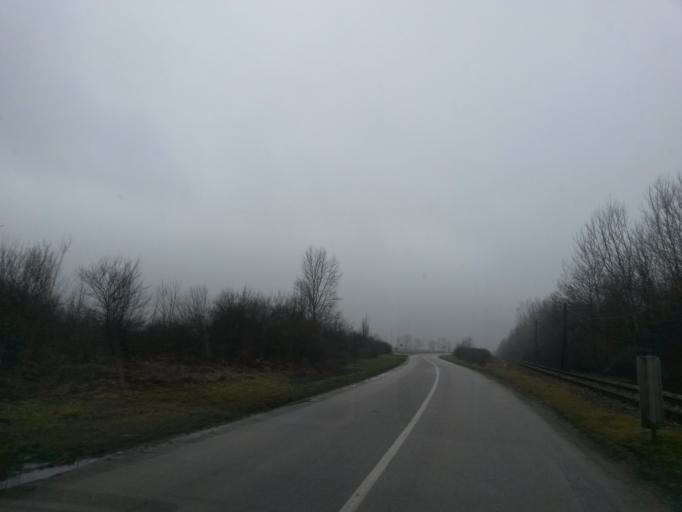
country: HR
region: Vukovarsko-Srijemska
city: Zupanja
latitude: 45.1067
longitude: 18.6995
